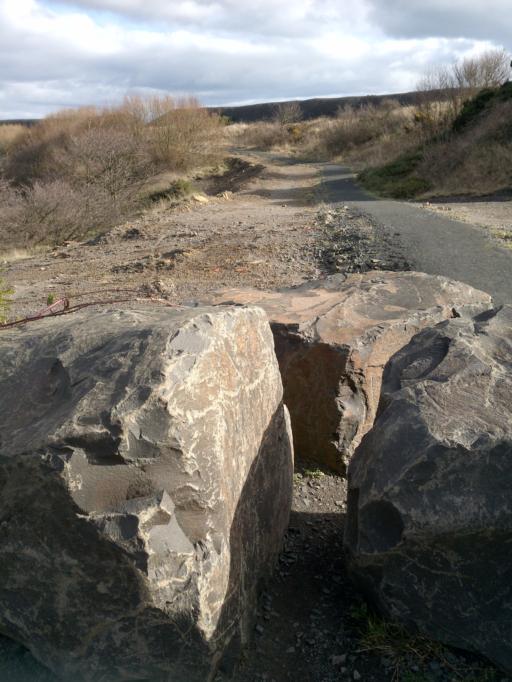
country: GB
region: England
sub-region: Northumberland
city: Lynemouth
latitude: 55.2093
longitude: -1.5269
